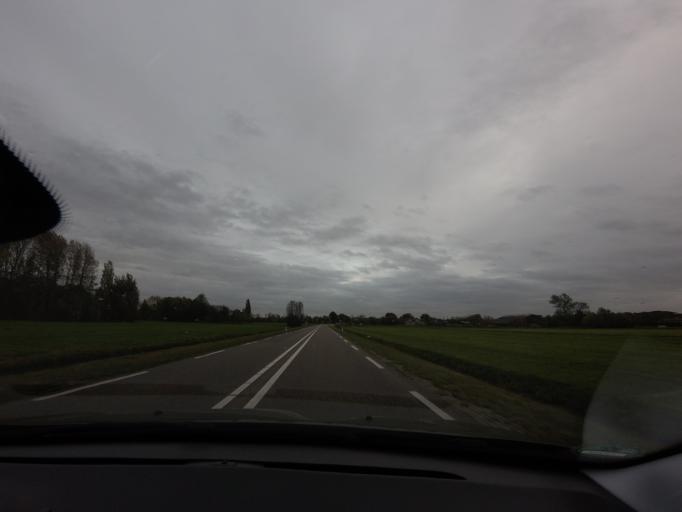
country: NL
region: Utrecht
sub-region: Gemeente Woerden
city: Woerden
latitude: 52.1082
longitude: 4.9182
